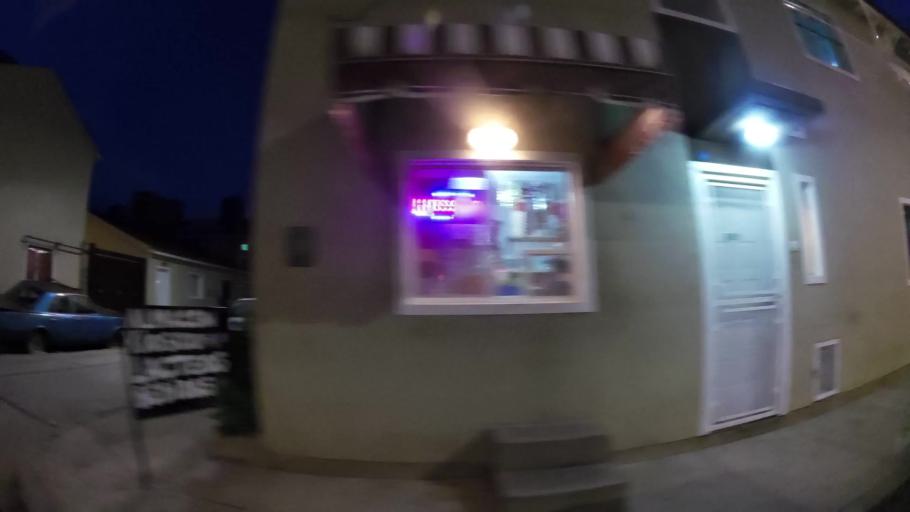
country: AR
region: Buenos Aires
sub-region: Partido de Quilmes
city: Quilmes
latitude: -34.7009
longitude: -58.3064
